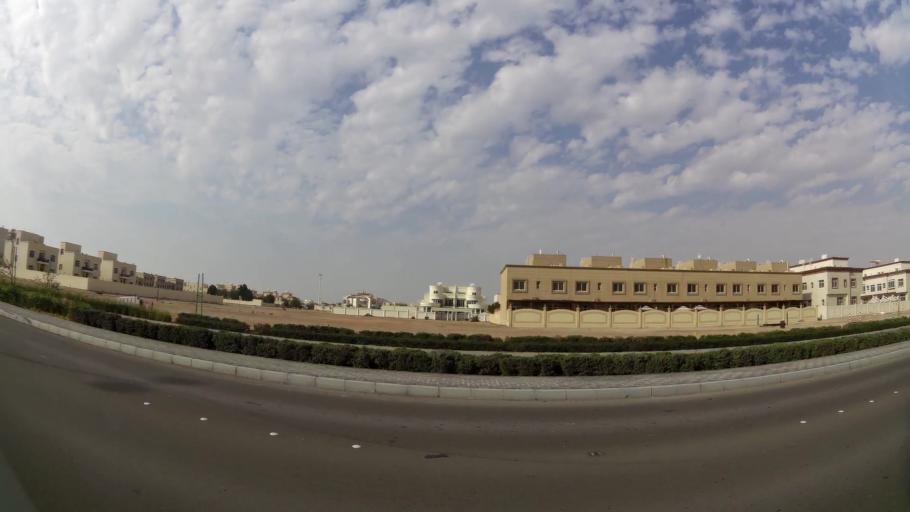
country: AE
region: Abu Dhabi
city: Abu Dhabi
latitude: 24.3482
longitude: 54.5597
